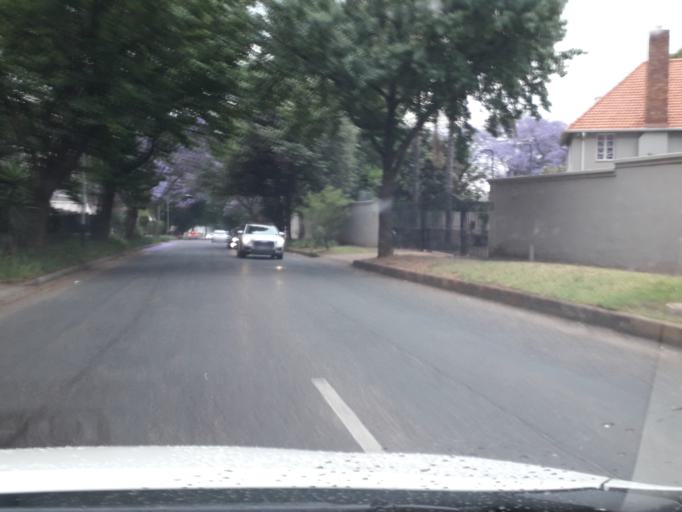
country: ZA
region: Gauteng
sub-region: City of Johannesburg Metropolitan Municipality
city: Johannesburg
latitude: -26.1473
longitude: 28.0464
